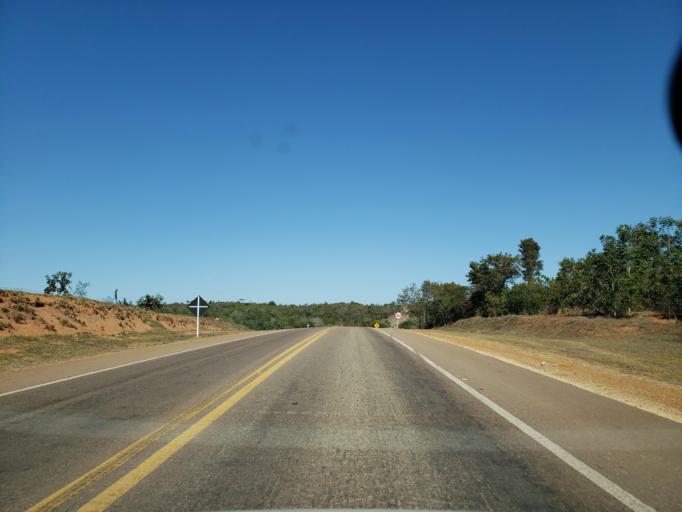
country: BR
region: Mato Grosso
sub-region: Poxoreo
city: Poxoreo
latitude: -15.7801
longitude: -54.3681
